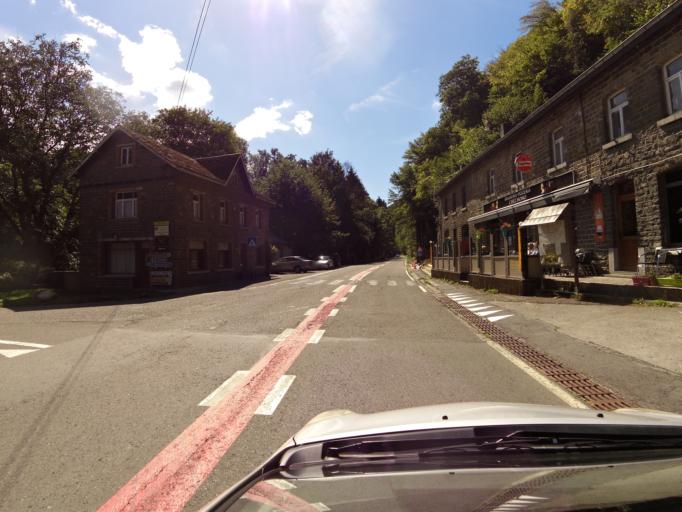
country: BE
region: Wallonia
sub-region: Province du Luxembourg
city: Rendeux
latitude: 50.2159
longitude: 5.5195
